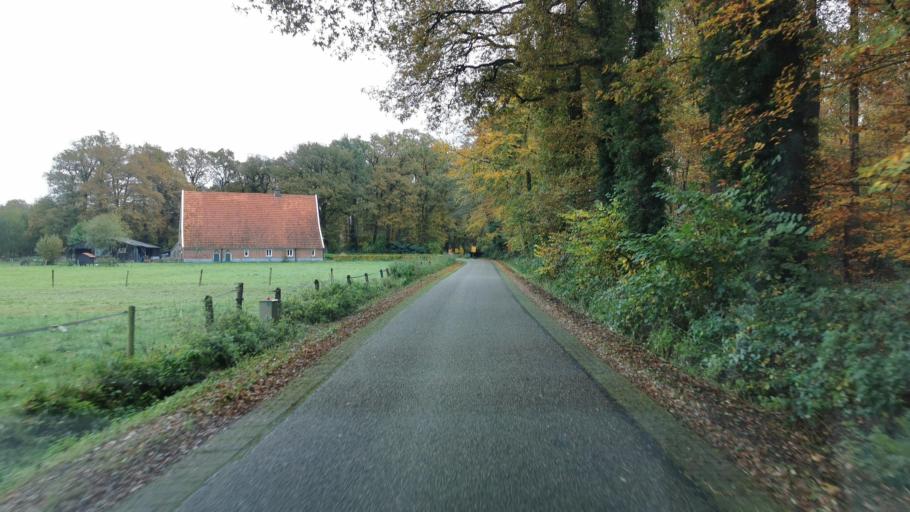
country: NL
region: Overijssel
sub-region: Gemeente Enschede
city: Enschede
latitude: 52.2075
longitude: 6.9243
